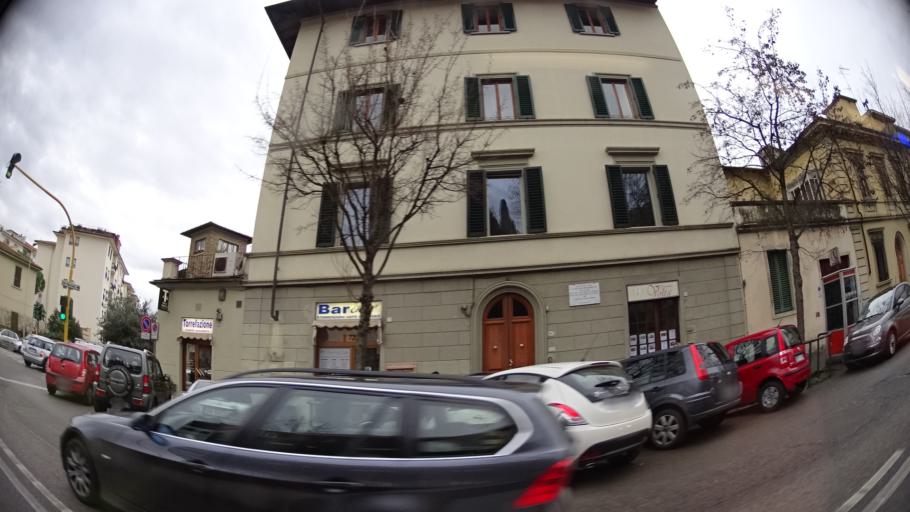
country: IT
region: Tuscany
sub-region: Province of Florence
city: Fiesole
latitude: 43.7862
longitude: 11.2752
